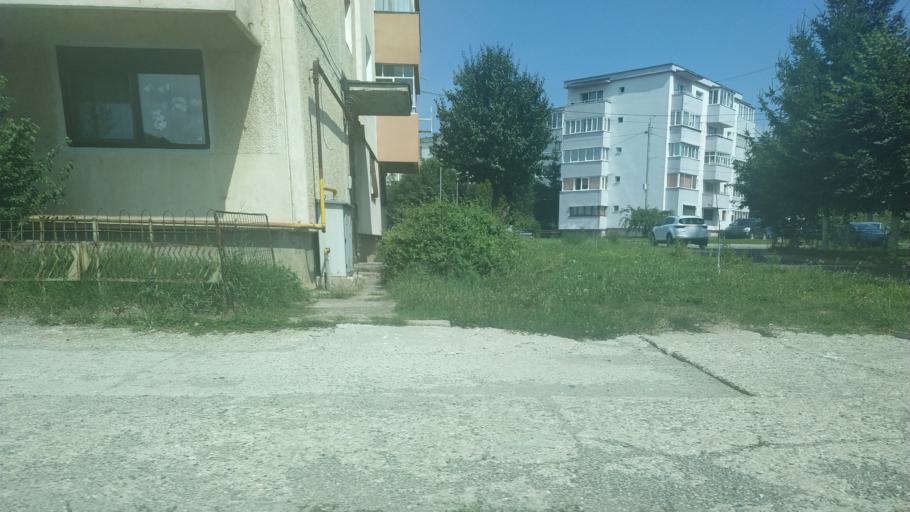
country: RO
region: Brasov
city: Fogarasch
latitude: 45.8402
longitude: 24.9666
